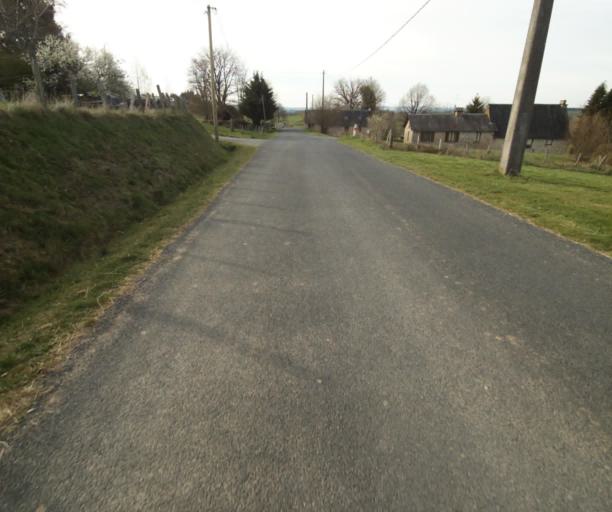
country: FR
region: Limousin
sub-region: Departement de la Correze
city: Chamboulive
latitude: 45.4379
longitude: 1.7824
